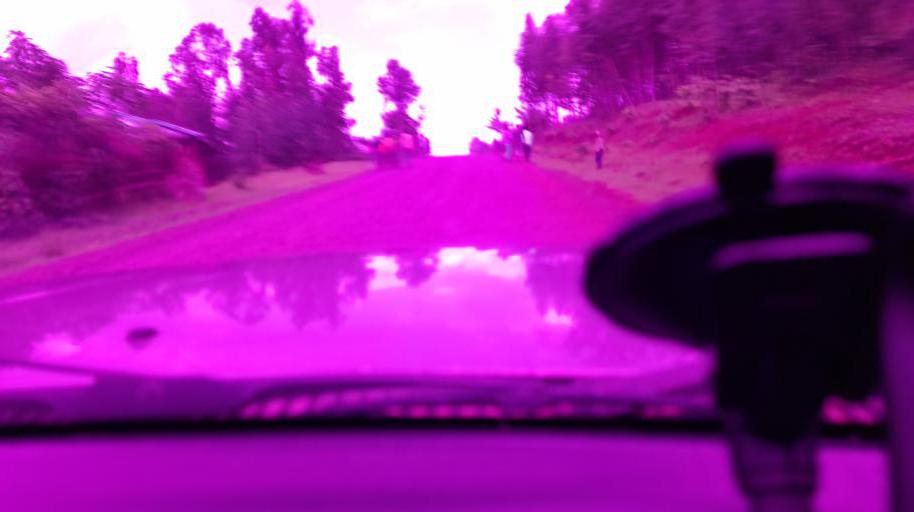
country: ET
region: Oromiya
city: Jima
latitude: 7.9895
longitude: 37.4828
